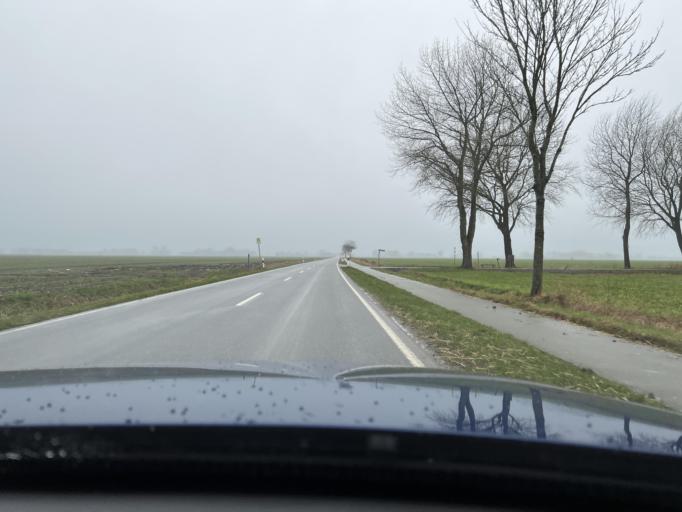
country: DE
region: Schleswig-Holstein
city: Stelle-Wittenwurth
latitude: 54.2421
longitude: 9.0306
